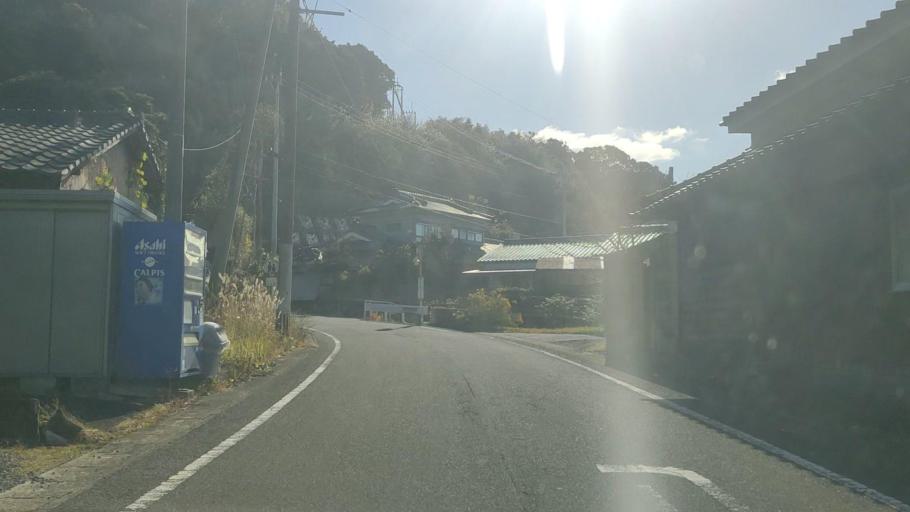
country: JP
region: Kagoshima
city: Kokubu-matsuki
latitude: 31.6711
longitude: 130.8197
